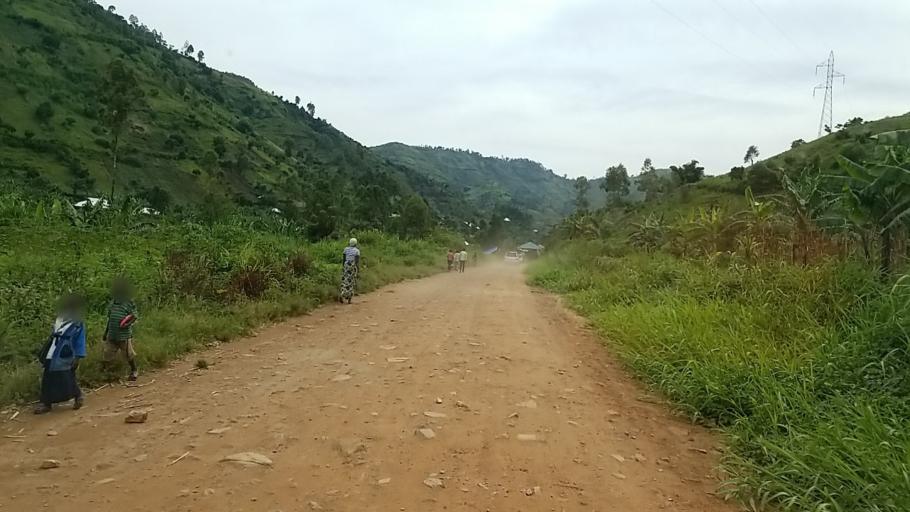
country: CD
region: Nord Kivu
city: Sake
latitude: -1.7245
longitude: 29.0109
